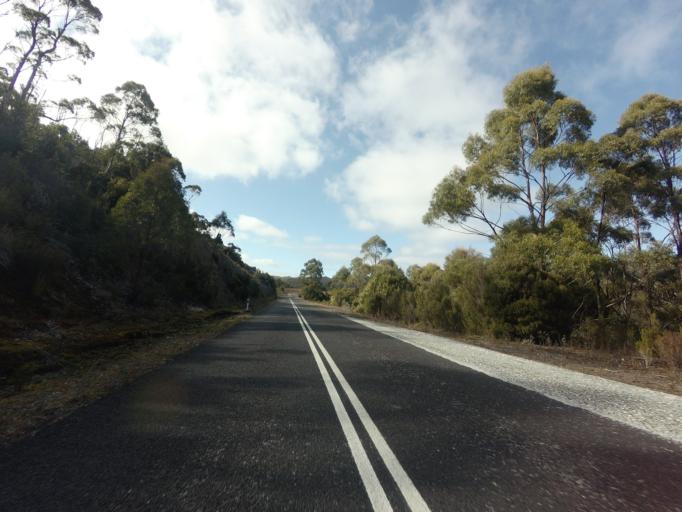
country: AU
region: Tasmania
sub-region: West Coast
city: Queenstown
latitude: -42.7969
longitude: 146.0873
